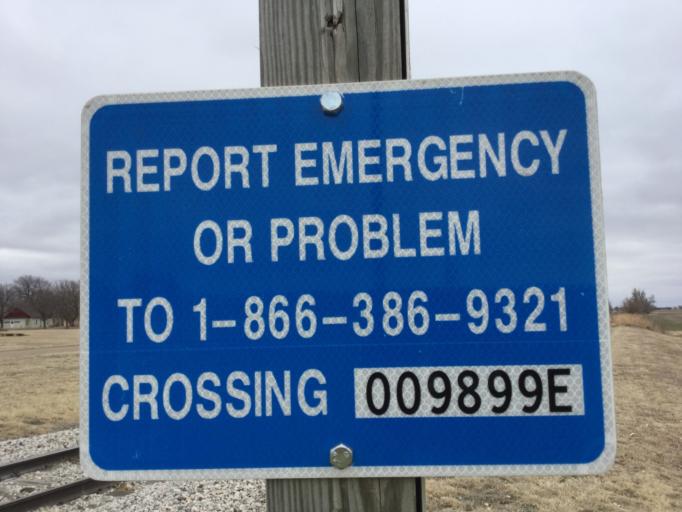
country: US
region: Kansas
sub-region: Barton County
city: Ellinwood
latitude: 38.2767
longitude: -98.4158
